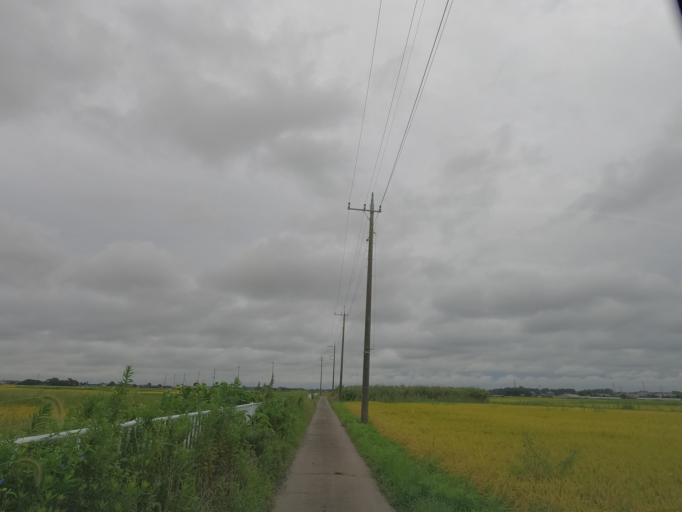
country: JP
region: Ibaraki
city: Toride
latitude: 35.9291
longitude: 140.0632
